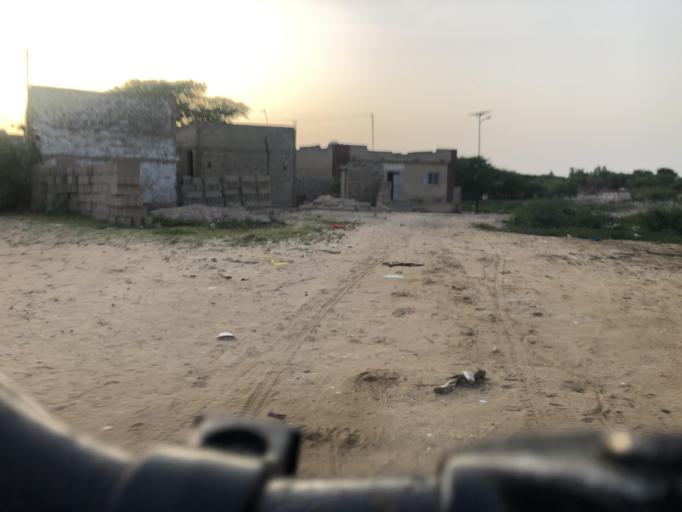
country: SN
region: Saint-Louis
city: Saint-Louis
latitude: 16.0700
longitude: -16.4281
